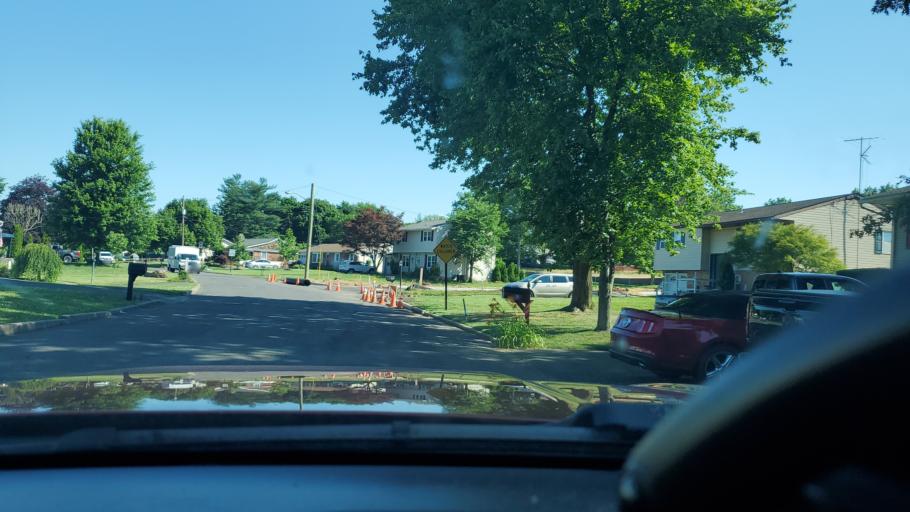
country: US
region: Pennsylvania
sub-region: Montgomery County
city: Pennsburg
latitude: 40.3870
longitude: -75.4933
